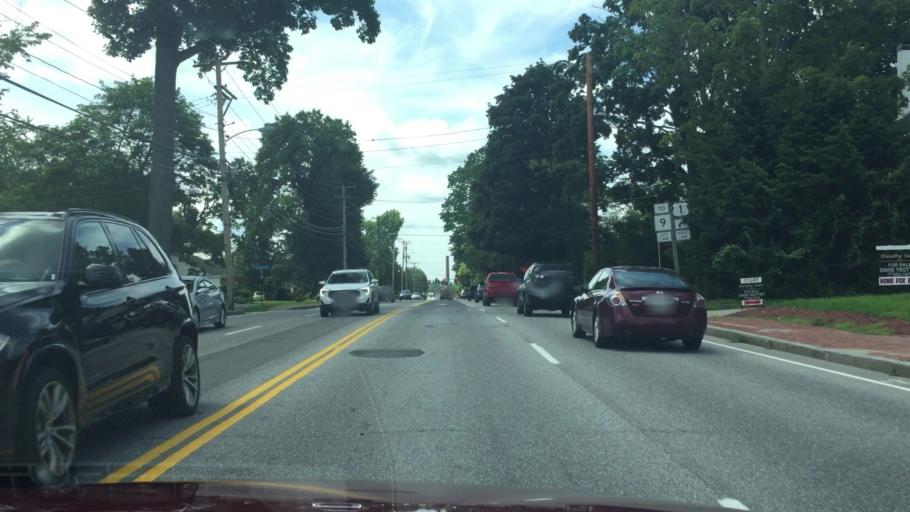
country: US
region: Maine
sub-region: York County
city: Saco
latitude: 43.5032
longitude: -70.4407
